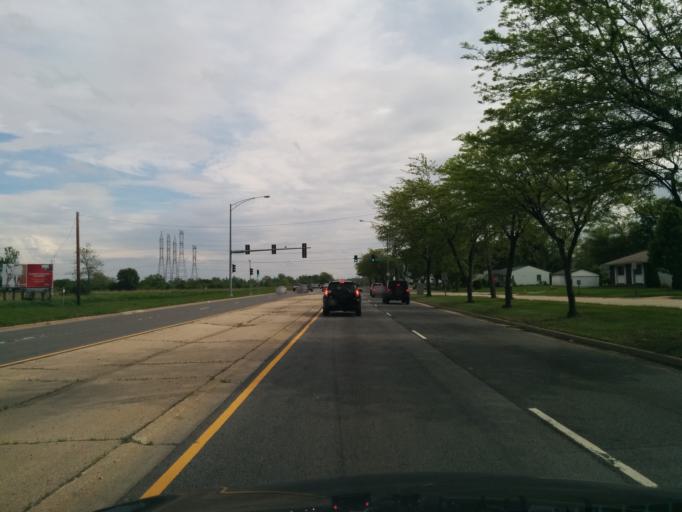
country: US
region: Illinois
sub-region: Will County
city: Romeoville
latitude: 41.6359
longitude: -88.0805
